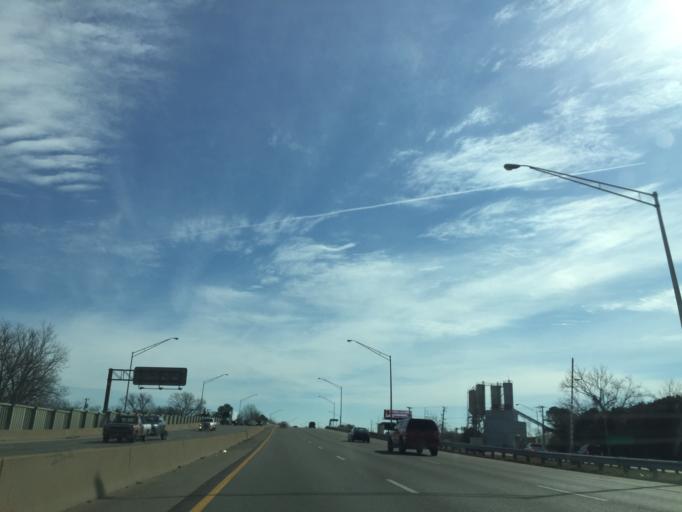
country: US
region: Virginia
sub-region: City of Hampton
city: Hampton
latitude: 37.0349
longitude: -76.3555
